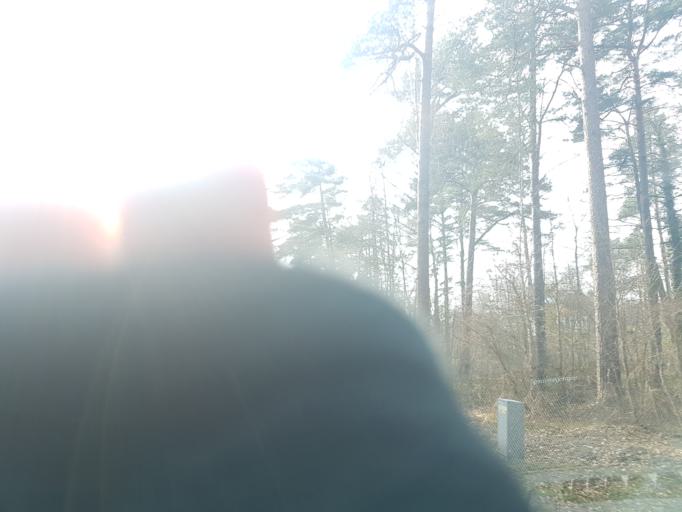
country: SE
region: Skane
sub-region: Ystads Kommun
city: Ystad
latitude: 55.4286
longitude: 13.8511
